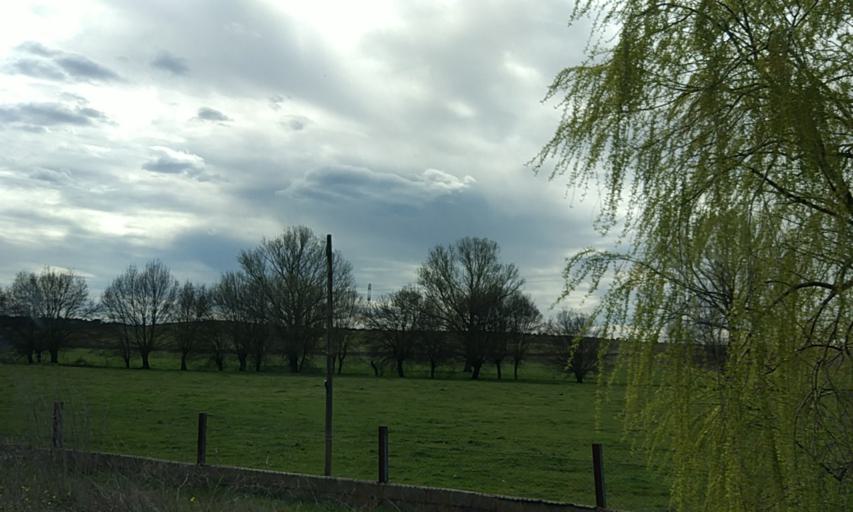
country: ES
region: Castille and Leon
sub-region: Provincia de Salamanca
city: Ciudad Rodrigo
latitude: 40.5593
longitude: -6.5541
